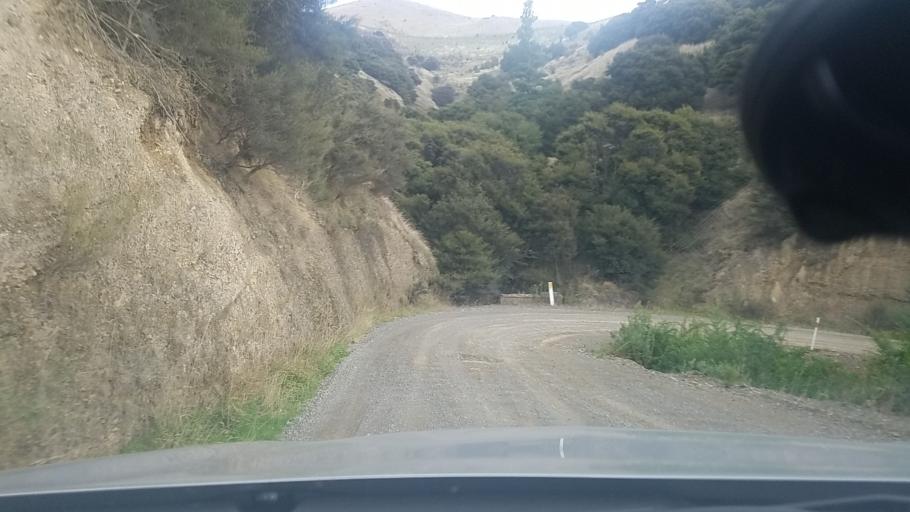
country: NZ
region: Marlborough
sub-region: Marlborough District
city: Blenheim
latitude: -41.5858
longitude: 174.0704
